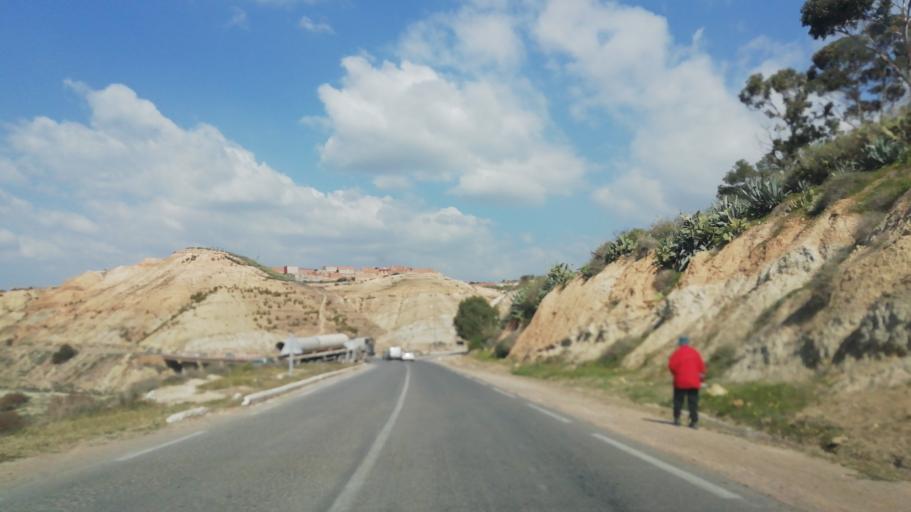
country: DZ
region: Mascara
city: Mascara
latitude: 35.5635
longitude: 0.0713
